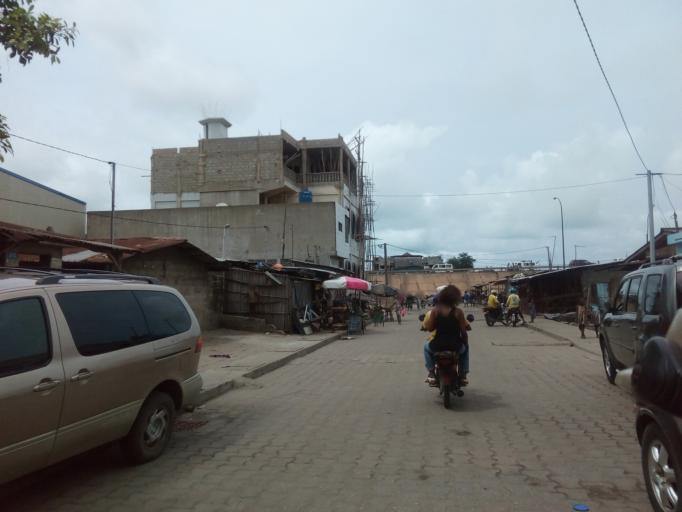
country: BJ
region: Littoral
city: Cotonou
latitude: 6.3724
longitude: 2.4393
